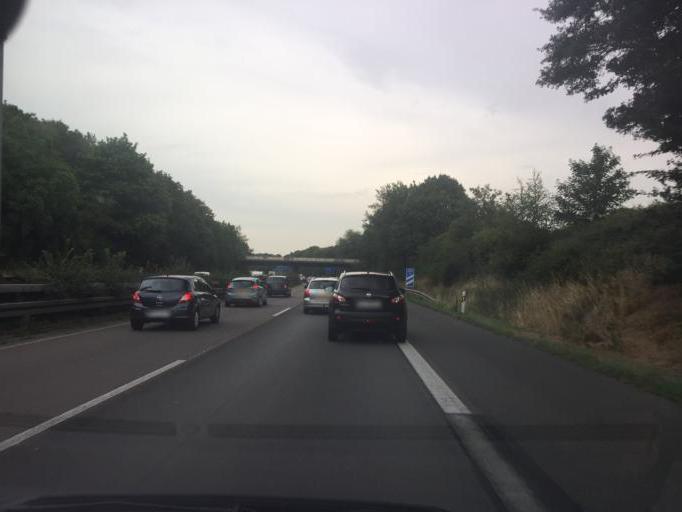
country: DE
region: North Rhine-Westphalia
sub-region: Regierungsbezirk Dusseldorf
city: Viersen
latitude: 51.1995
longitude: 6.3776
